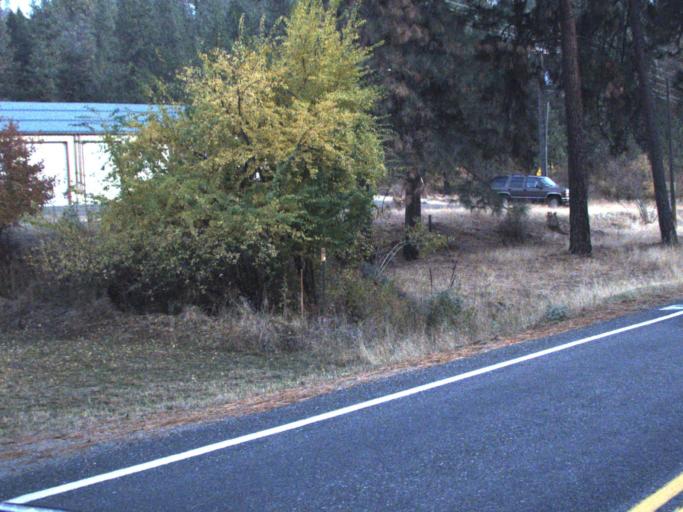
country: US
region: Washington
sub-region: Stevens County
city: Kettle Falls
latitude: 48.2796
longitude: -118.1362
